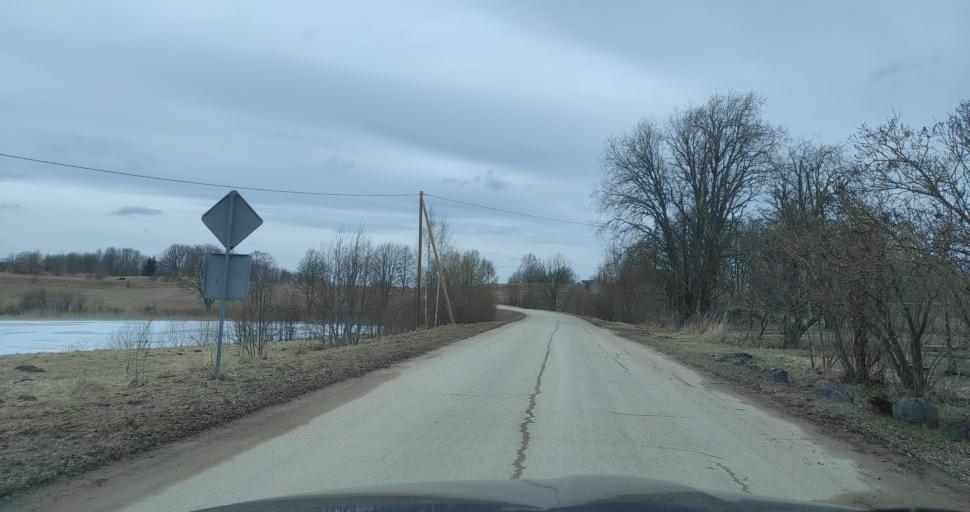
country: LV
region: Tukuma Rajons
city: Tukums
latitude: 57.0913
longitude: 23.0927
